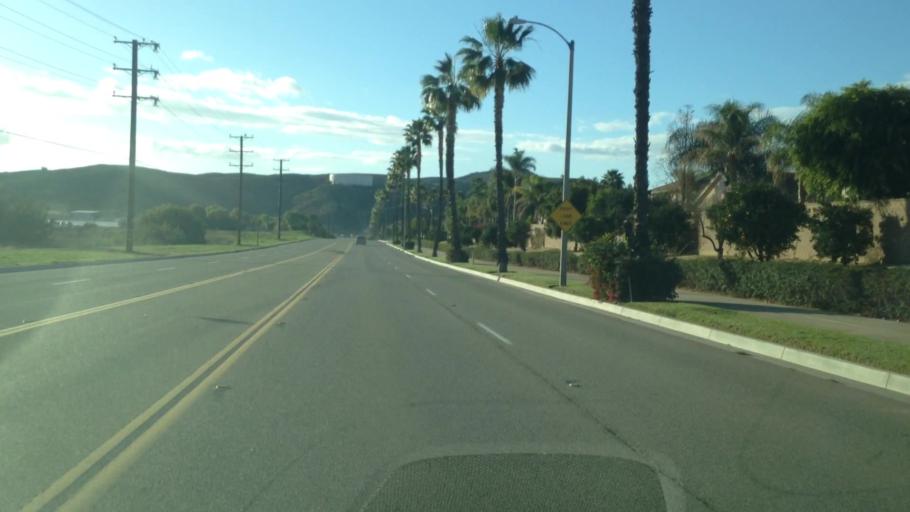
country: US
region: California
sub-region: Riverside County
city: Home Gardens
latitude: 33.8583
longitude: -117.4431
